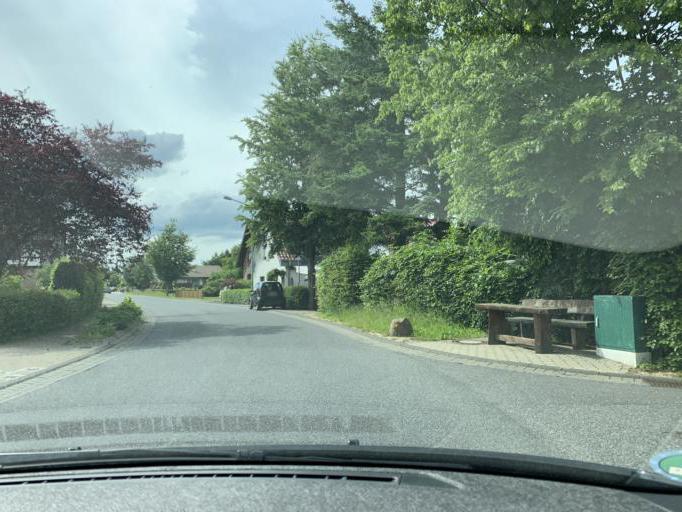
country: DE
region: North Rhine-Westphalia
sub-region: Regierungsbezirk Koln
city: Hurtgenwald
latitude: 50.6857
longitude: 6.3542
